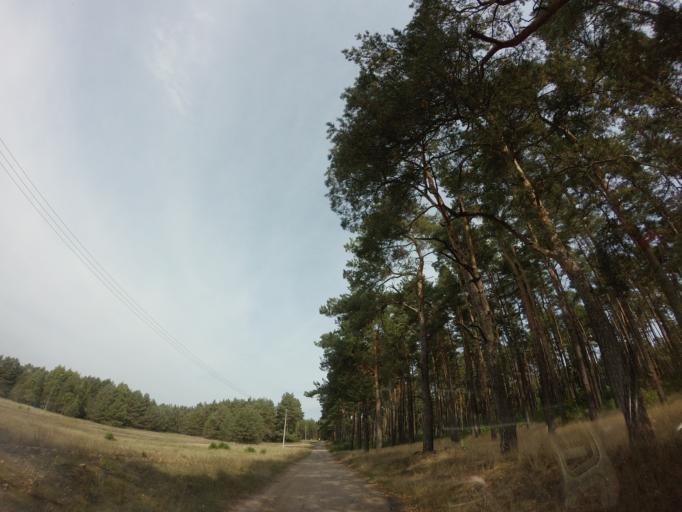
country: PL
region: West Pomeranian Voivodeship
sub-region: Powiat drawski
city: Drawsko Pomorskie
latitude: 53.4688
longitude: 15.7136
